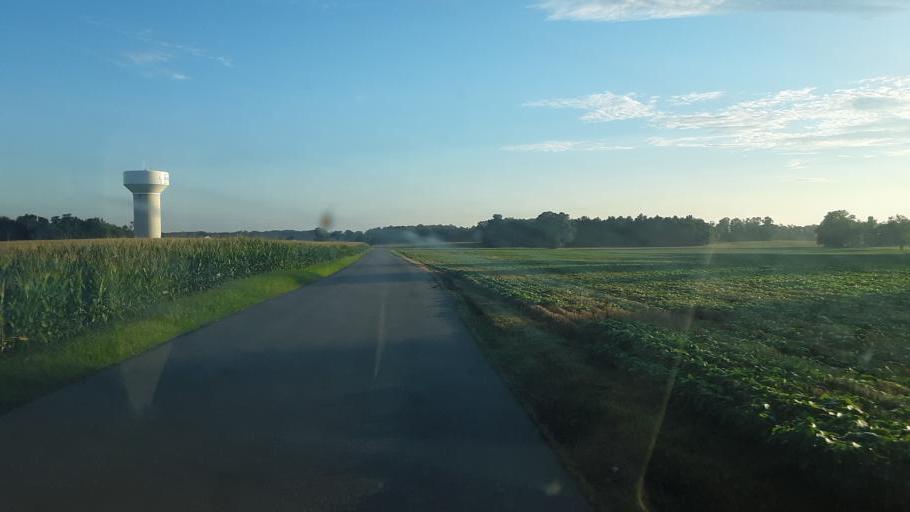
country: US
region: Kentucky
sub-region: Todd County
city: Guthrie
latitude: 36.7017
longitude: -87.1701
